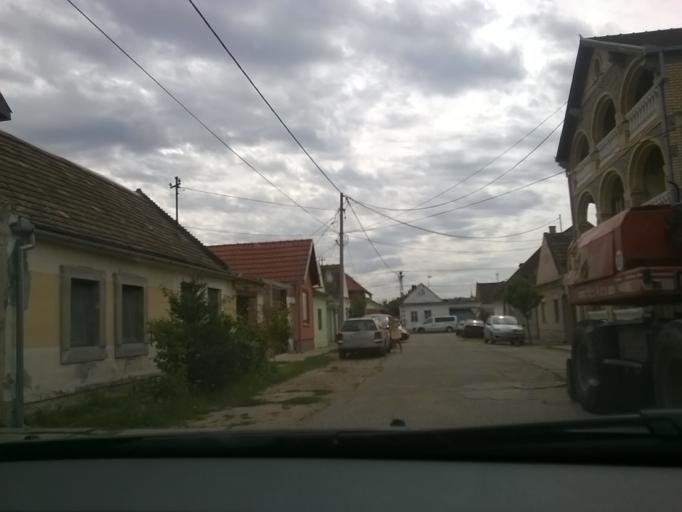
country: RS
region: Autonomna Pokrajina Vojvodina
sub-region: Juznobanatski Okrug
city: Vrsac
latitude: 45.1282
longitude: 21.2954
